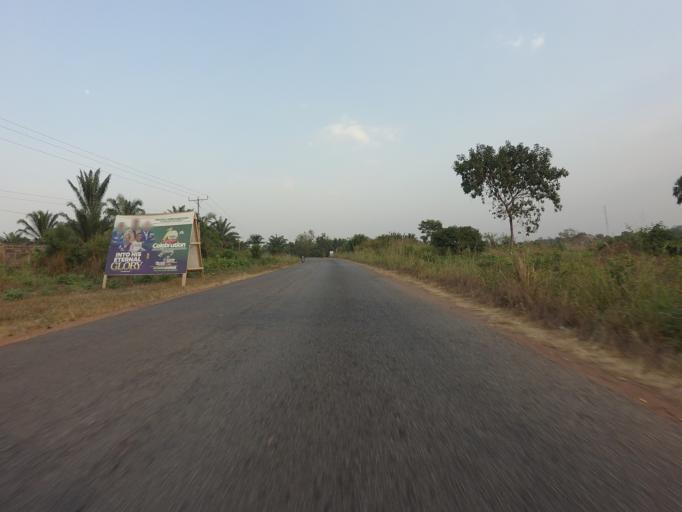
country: GH
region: Volta
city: Ho
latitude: 6.5701
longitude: 0.3903
